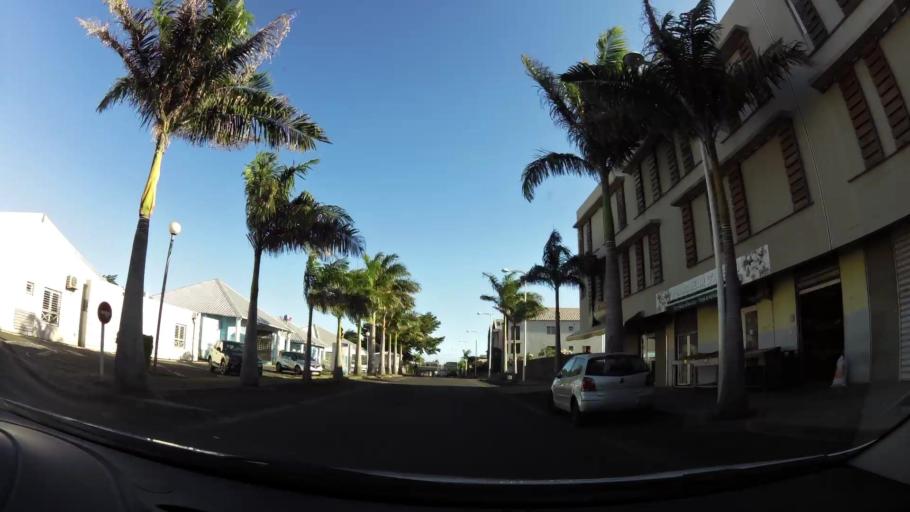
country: RE
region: Reunion
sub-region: Reunion
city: Saint-Louis
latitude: -21.2897
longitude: 55.4041
